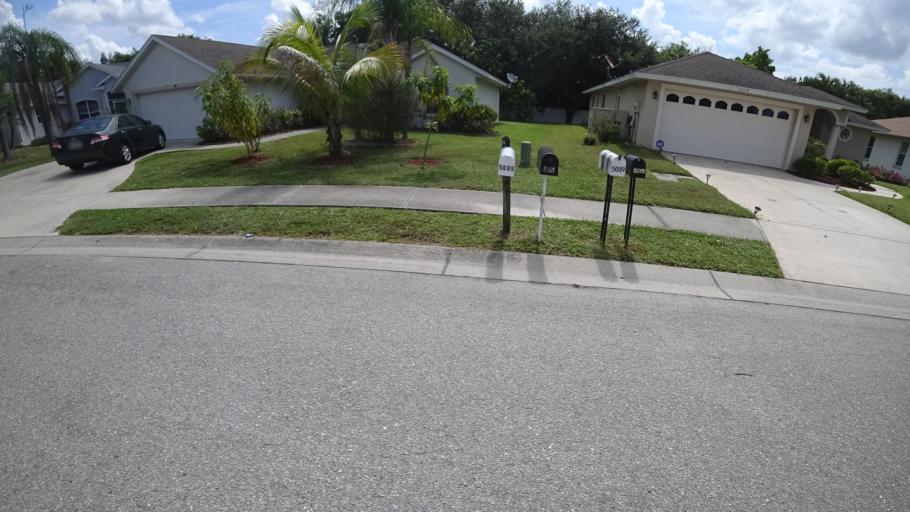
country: US
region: Florida
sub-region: Manatee County
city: Samoset
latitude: 27.4528
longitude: -82.5335
